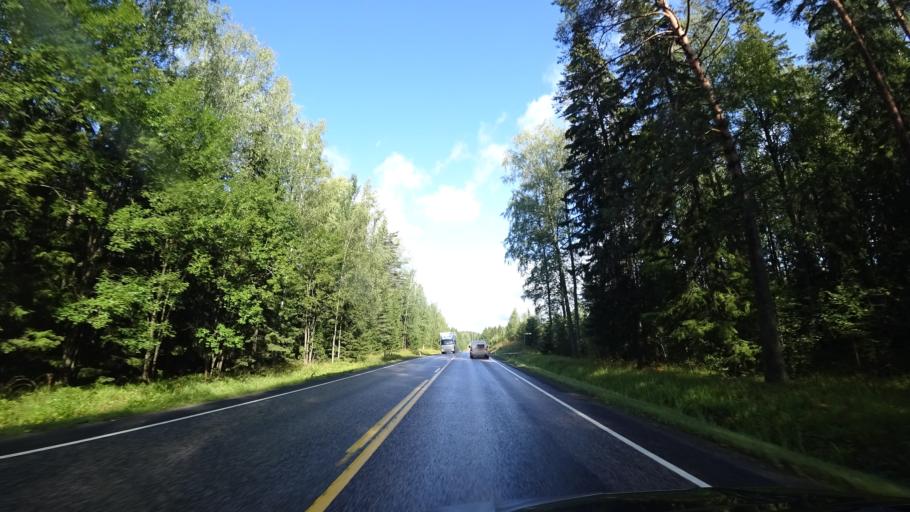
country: FI
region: Uusimaa
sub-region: Helsinki
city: Tuusula
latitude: 60.4518
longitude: 24.9573
